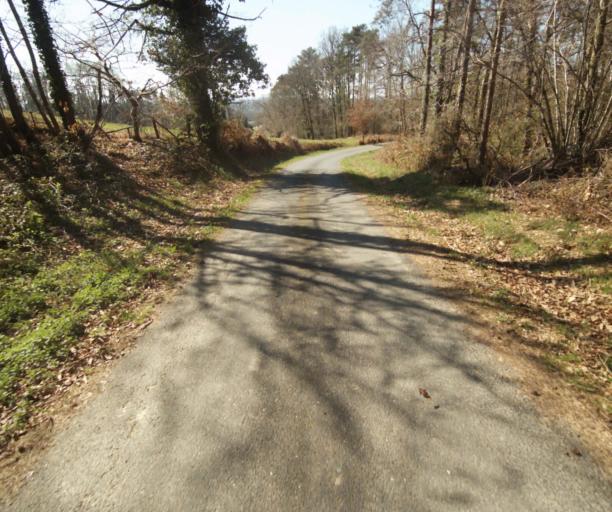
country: FR
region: Limousin
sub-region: Departement de la Correze
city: Saint-Mexant
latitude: 45.3105
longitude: 1.6094
